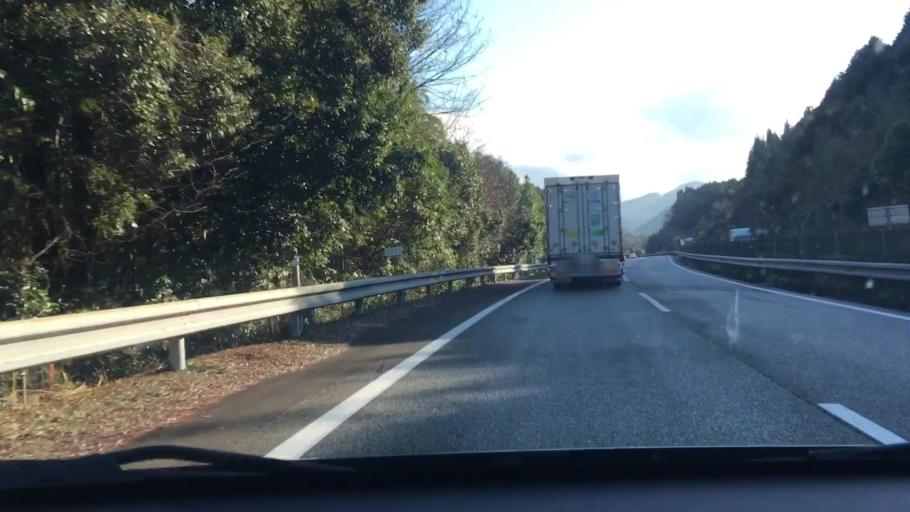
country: JP
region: Kumamoto
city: Hitoyoshi
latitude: 32.1683
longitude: 130.7928
